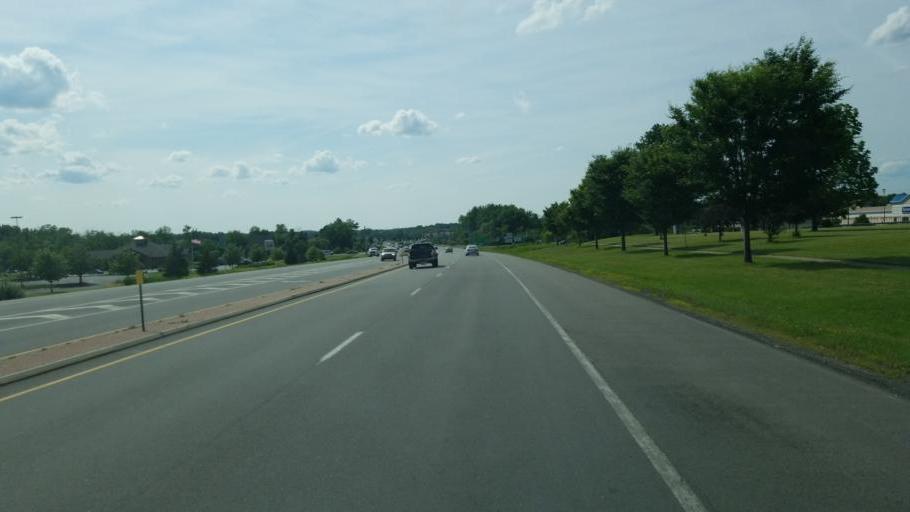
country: US
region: New York
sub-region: Ontario County
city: Canandaigua
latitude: 42.8752
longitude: -77.2464
